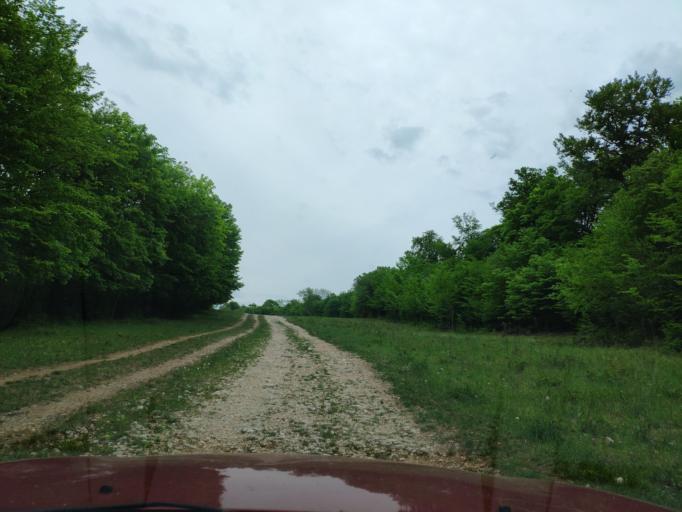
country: SK
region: Kosicky
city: Roznava
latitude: 48.5441
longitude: 20.5611
